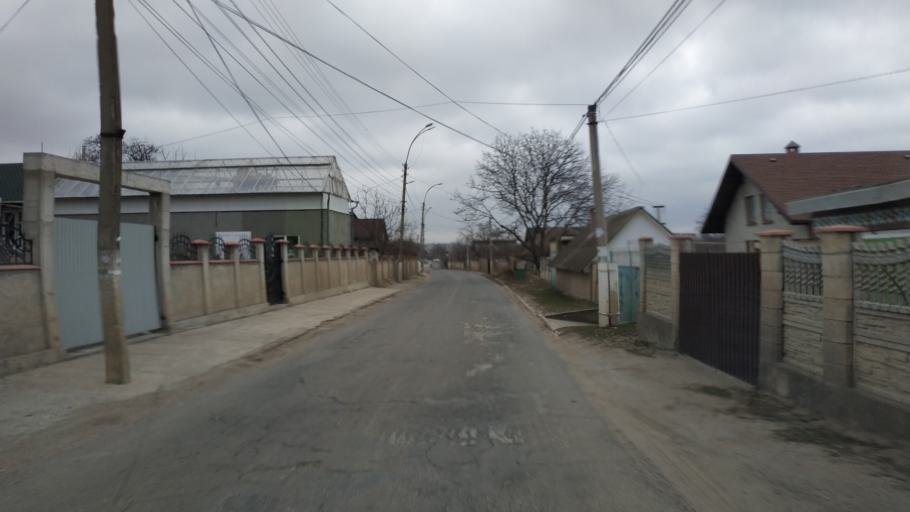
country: MD
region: Laloveni
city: Ialoveni
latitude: 46.9046
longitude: 28.8077
